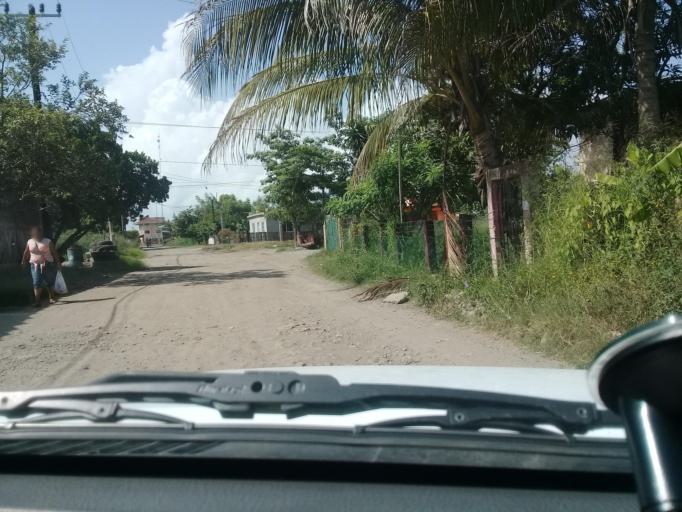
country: MX
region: Veracruz
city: Moralillo
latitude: 22.2263
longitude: -97.9032
